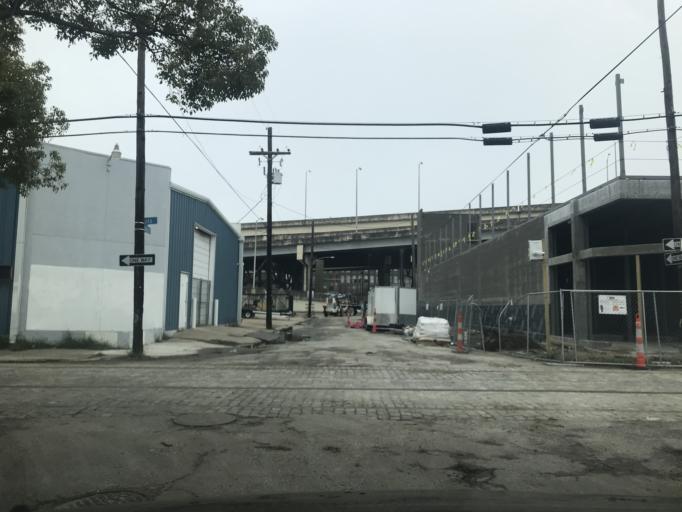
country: US
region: Louisiana
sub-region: Orleans Parish
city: New Orleans
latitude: 29.9390
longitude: -90.0699
